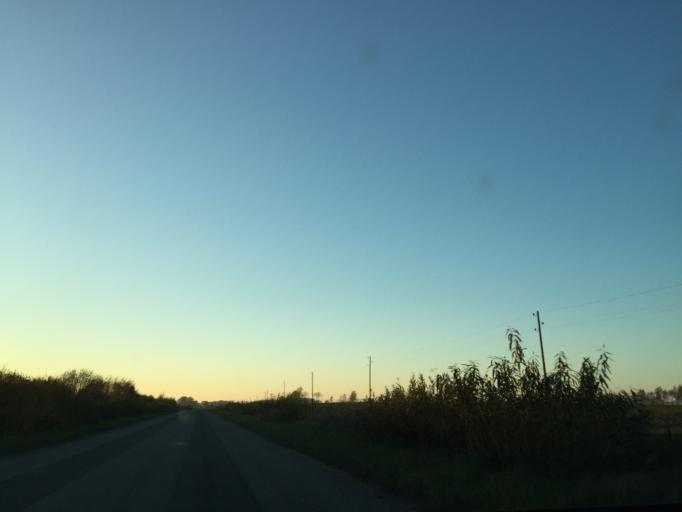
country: LT
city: Vieksniai
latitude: 56.3993
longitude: 22.5465
